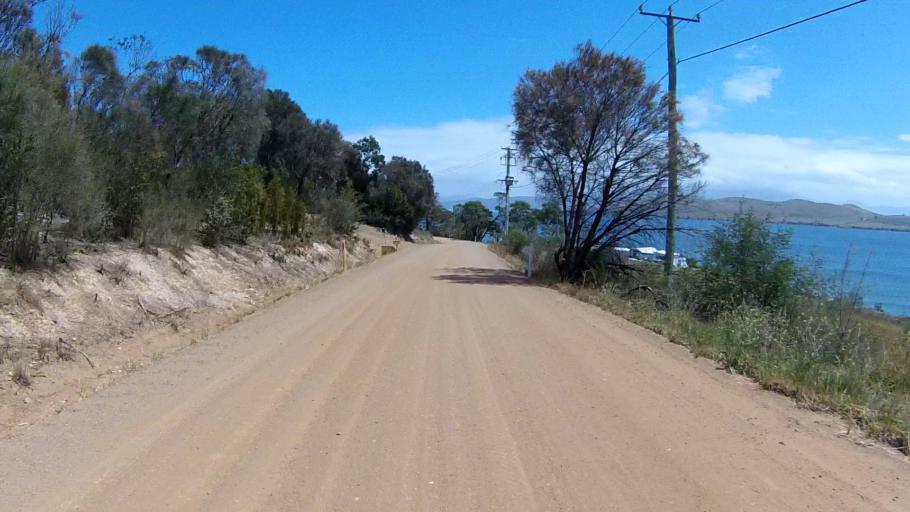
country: AU
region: Tasmania
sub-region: Clarence
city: Lauderdale
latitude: -42.9337
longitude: 147.4650
